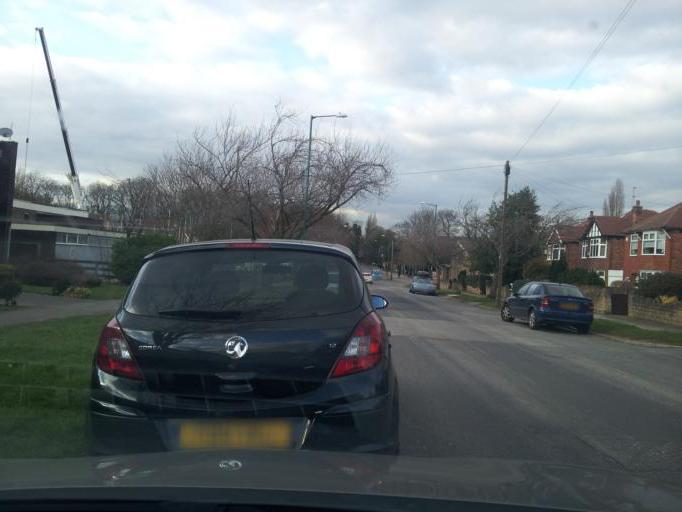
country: GB
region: England
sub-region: Nottingham
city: Nottingham
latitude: 52.9560
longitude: -1.2086
